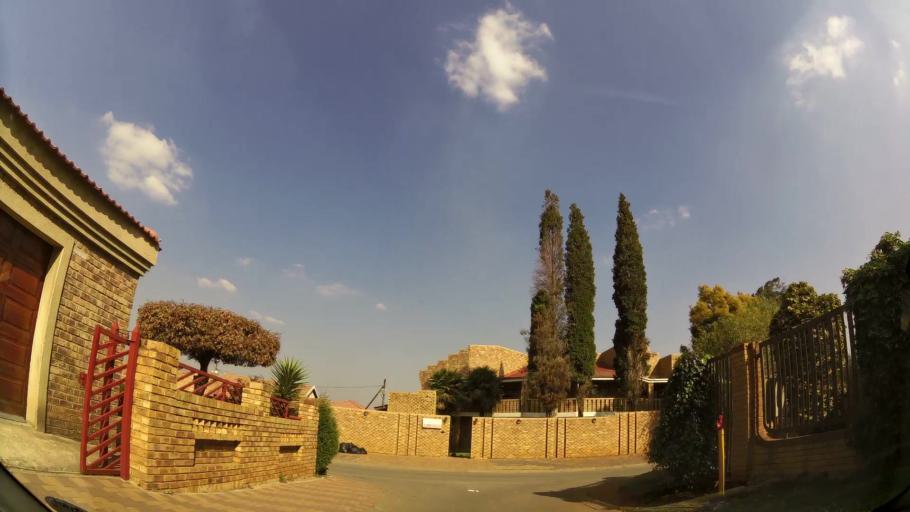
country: ZA
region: Gauteng
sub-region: Ekurhuleni Metropolitan Municipality
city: Brakpan
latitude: -26.1603
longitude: 28.4039
